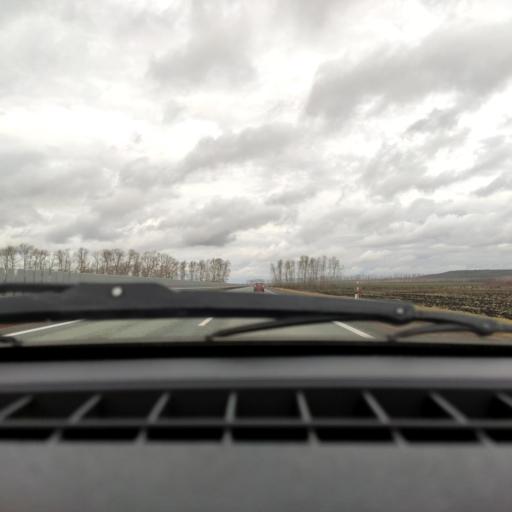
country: RU
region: Bashkortostan
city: Asanovo
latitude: 54.9452
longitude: 55.5821
